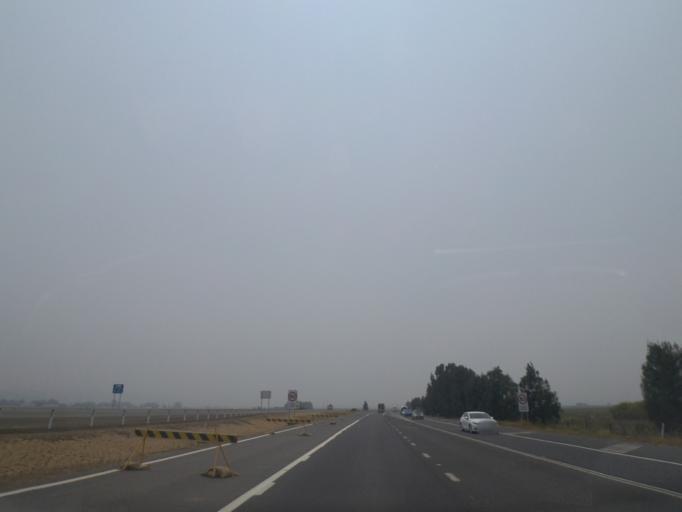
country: AU
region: New South Wales
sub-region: Clarence Valley
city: Maclean
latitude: -29.3916
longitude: 153.2399
